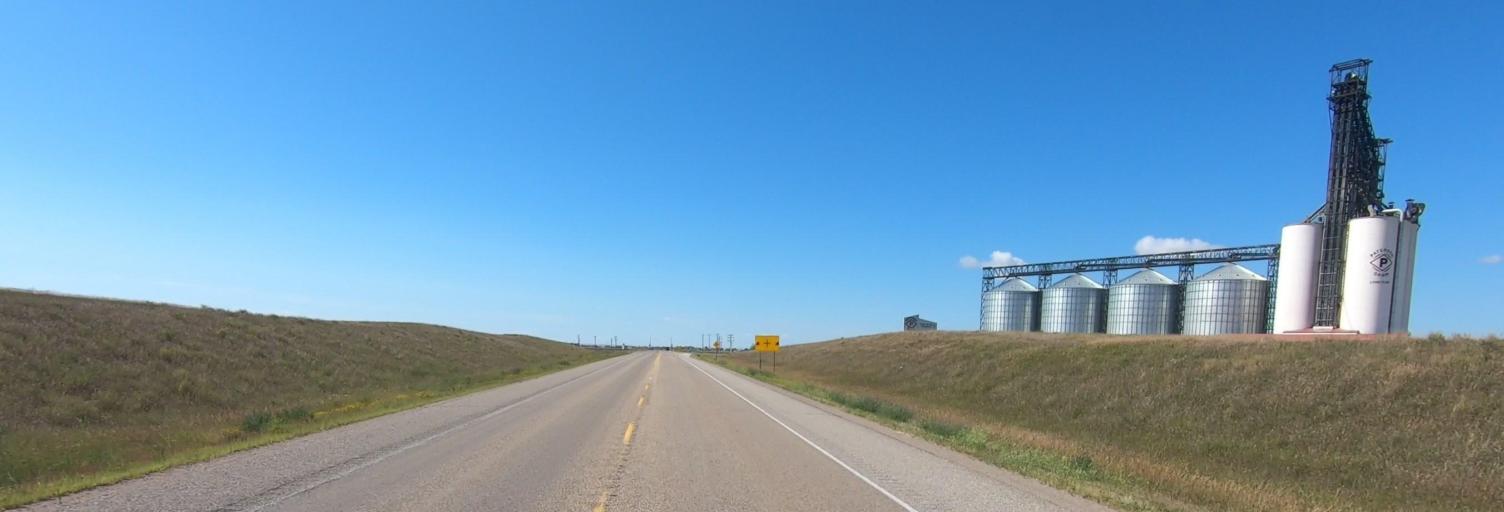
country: CA
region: Alberta
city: Strathmore
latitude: 50.8579
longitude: -113.0114
